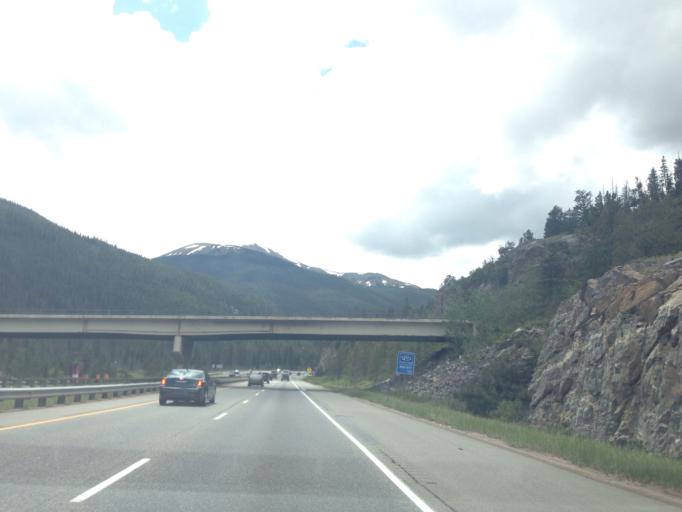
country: US
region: Colorado
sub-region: Clear Creek County
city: Georgetown
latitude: 39.6929
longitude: -105.8045
